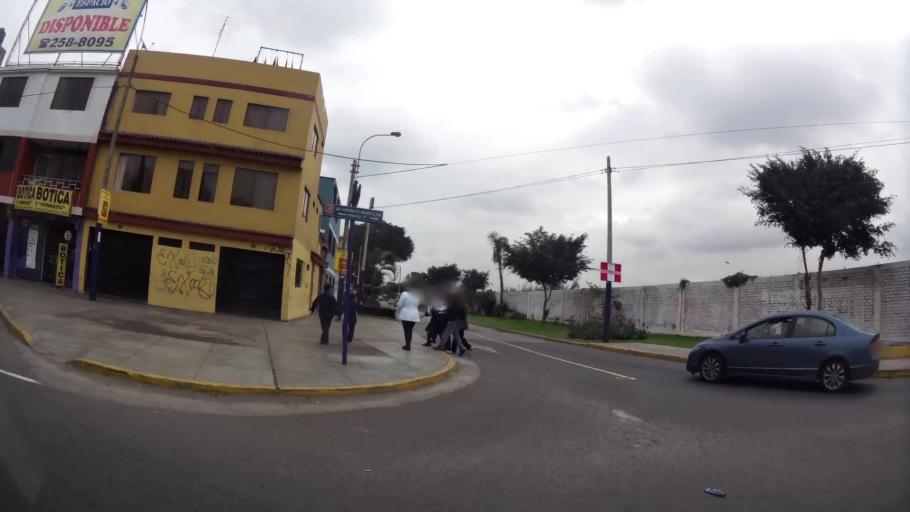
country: PE
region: Lima
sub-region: Lima
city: Surco
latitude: -12.1734
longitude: -77.0050
